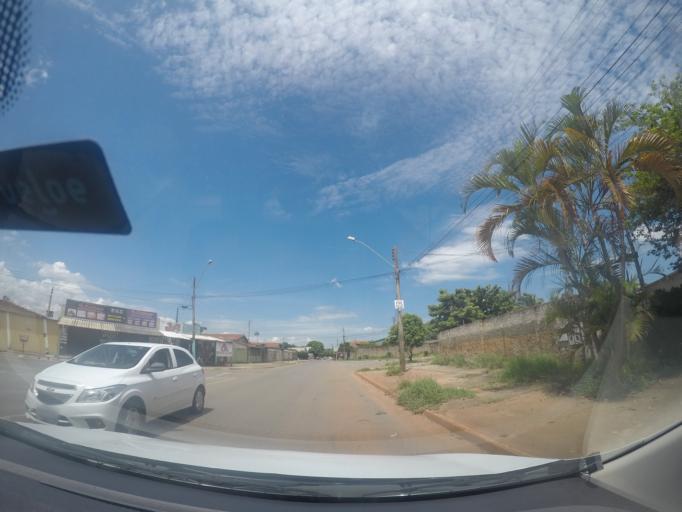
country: BR
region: Goias
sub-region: Goiania
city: Goiania
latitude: -16.6887
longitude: -49.3494
